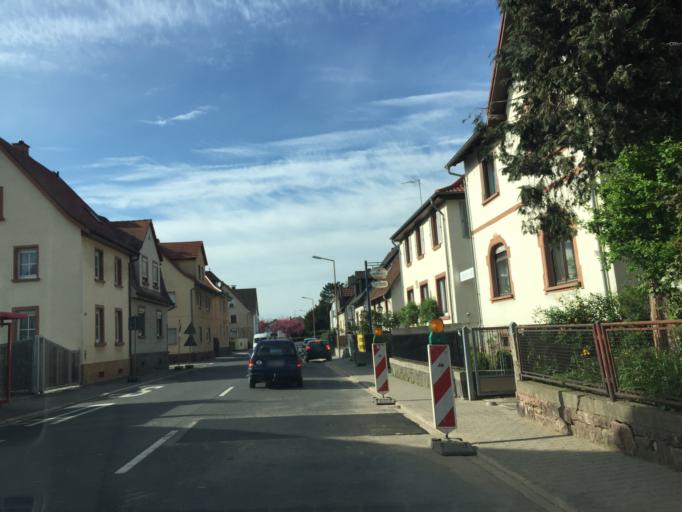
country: DE
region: Baden-Wuerttemberg
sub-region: Karlsruhe Region
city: Hemsbach
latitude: 49.5804
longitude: 8.6587
